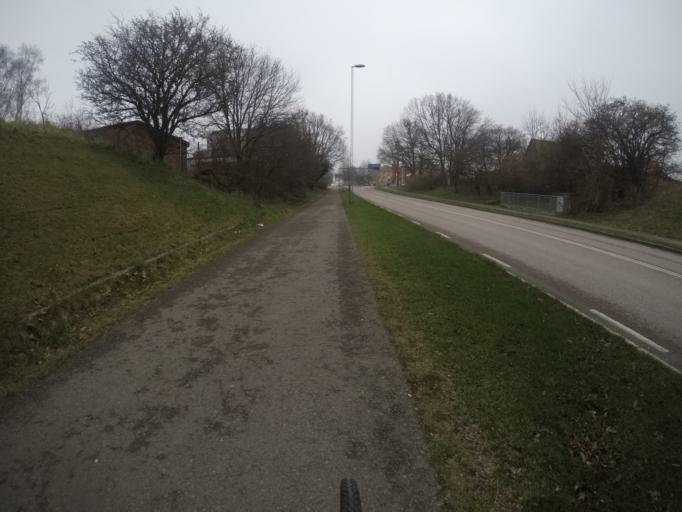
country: SE
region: Skane
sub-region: Hoganas Kommun
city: Hoganas
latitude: 56.2015
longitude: 12.5641
